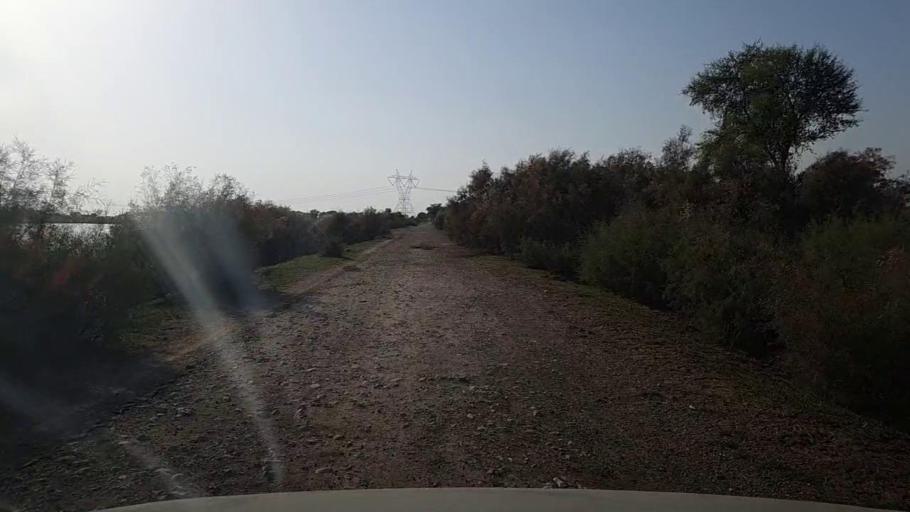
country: PK
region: Sindh
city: Kandhkot
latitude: 28.2907
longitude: 69.3241
